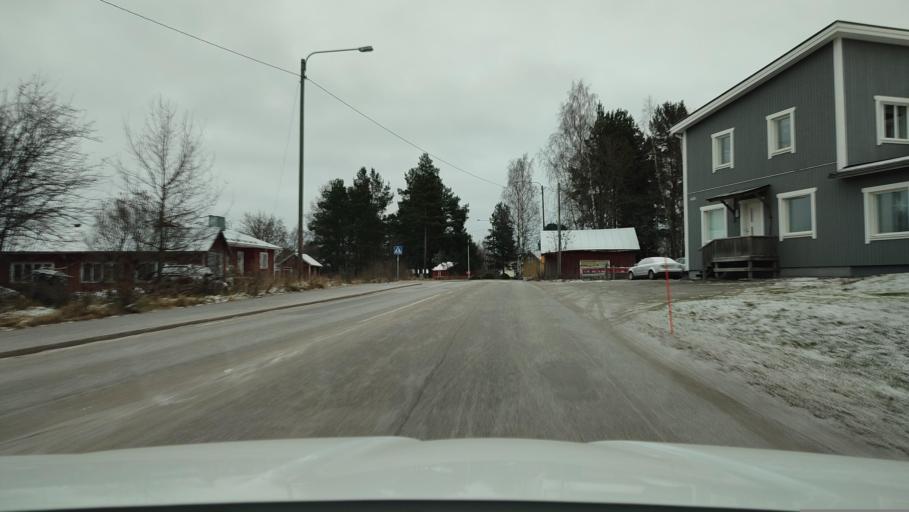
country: FI
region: Ostrobothnia
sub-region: Vaasa
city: Smedsby
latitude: 63.1545
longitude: 21.6921
